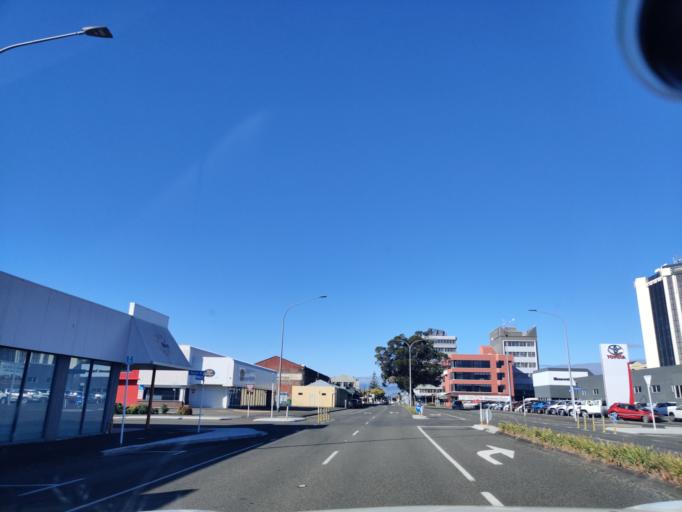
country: NZ
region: Manawatu-Wanganui
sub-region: Palmerston North City
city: Palmerston North
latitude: -40.3539
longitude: 175.6066
